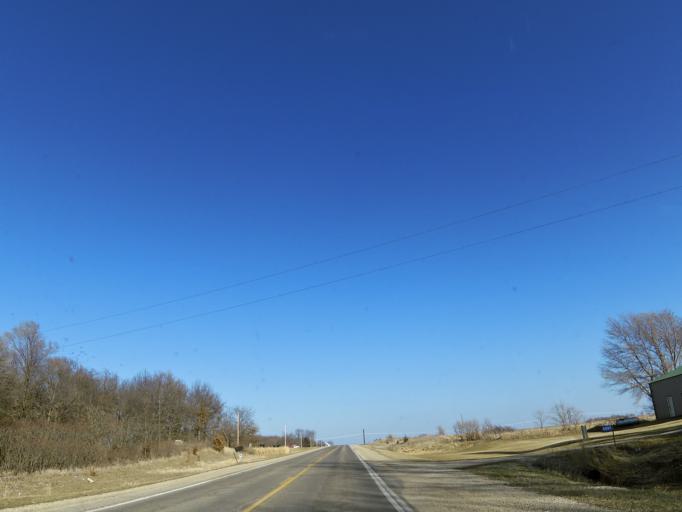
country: US
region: Iowa
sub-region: Worth County
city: Northwood
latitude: 43.4443
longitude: -93.2982
